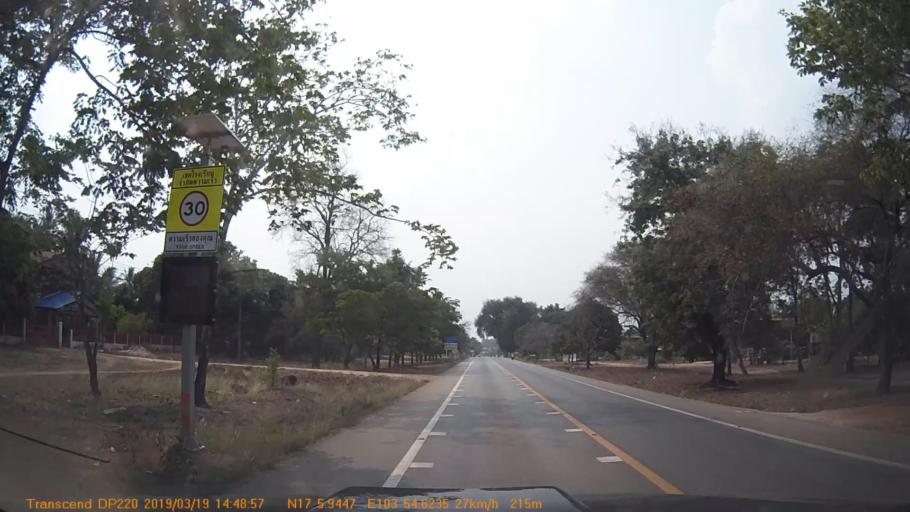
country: TH
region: Sakon Nakhon
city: Kut Bak
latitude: 17.0992
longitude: 103.9103
